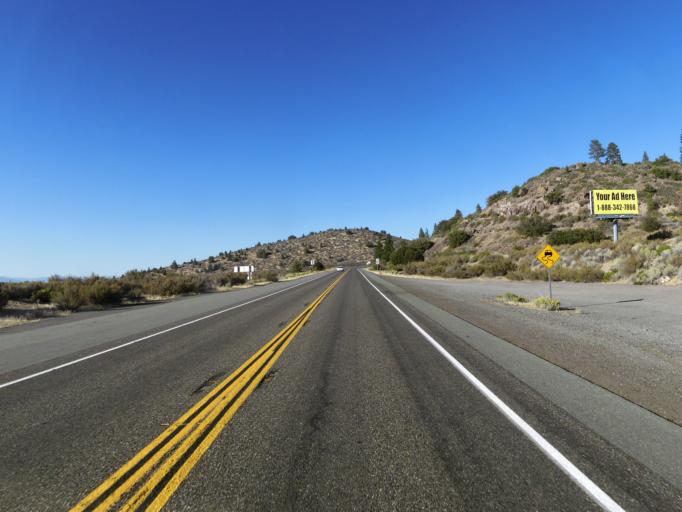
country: US
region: California
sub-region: Siskiyou County
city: Weed
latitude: 41.4739
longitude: -122.3512
